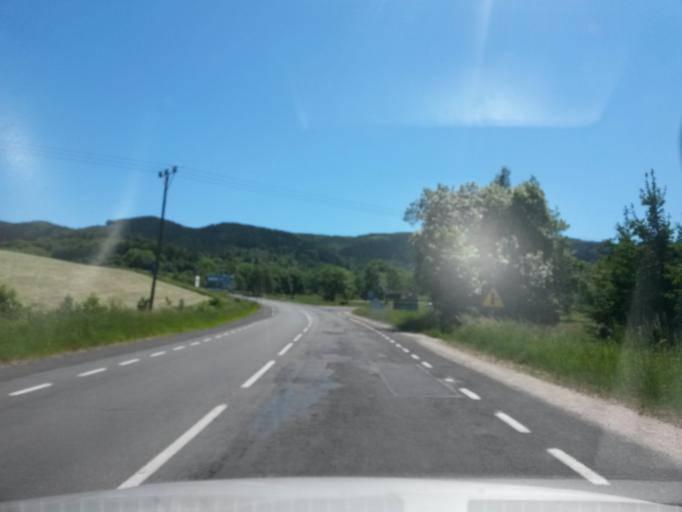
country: PL
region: Lower Silesian Voivodeship
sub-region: Powiat jeleniogorski
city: Kowary
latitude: 50.7919
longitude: 15.8513
